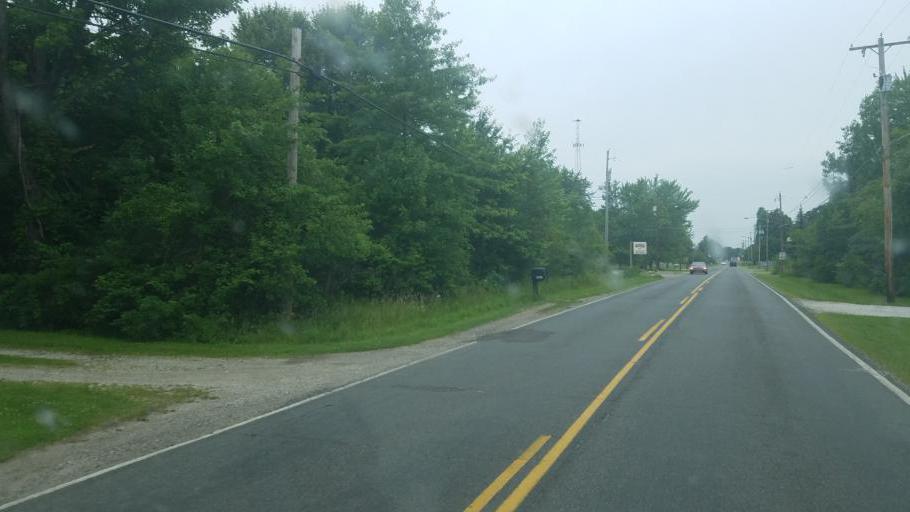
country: US
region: Ohio
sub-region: Portage County
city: Ravenna
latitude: 41.0996
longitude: -81.1396
